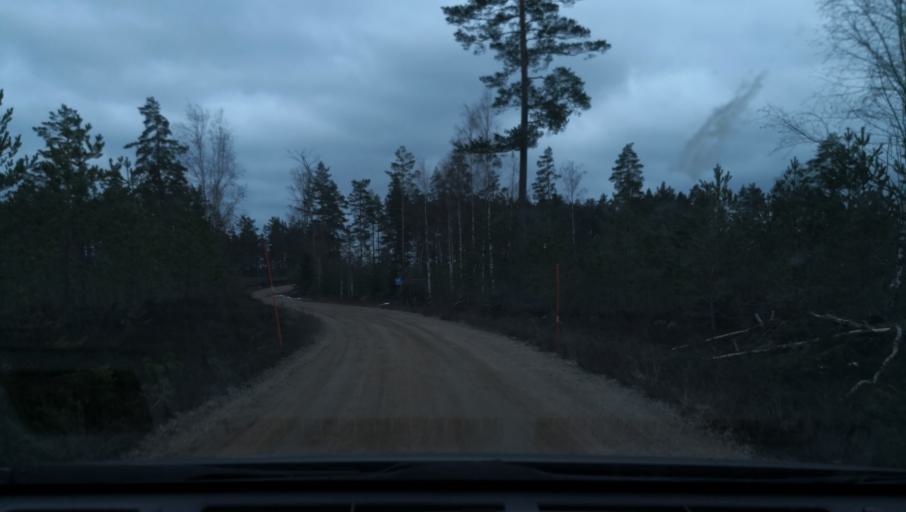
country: SE
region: OErebro
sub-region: Lindesbergs Kommun
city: Fellingsbro
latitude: 59.6038
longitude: 15.5784
